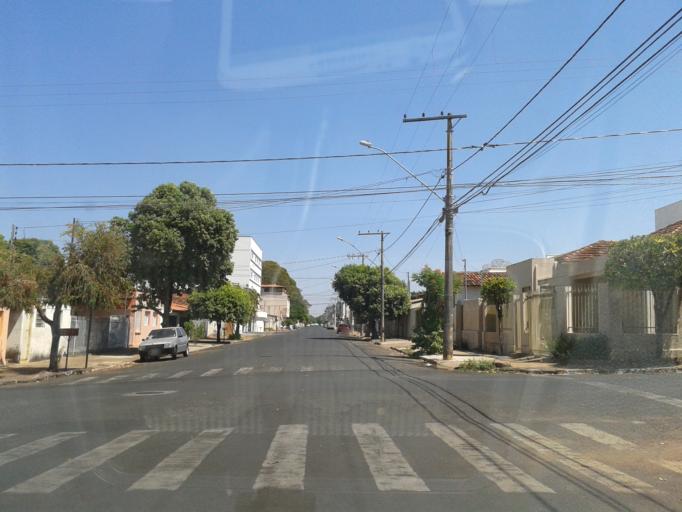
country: BR
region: Minas Gerais
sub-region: Araguari
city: Araguari
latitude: -18.6420
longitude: -48.1891
